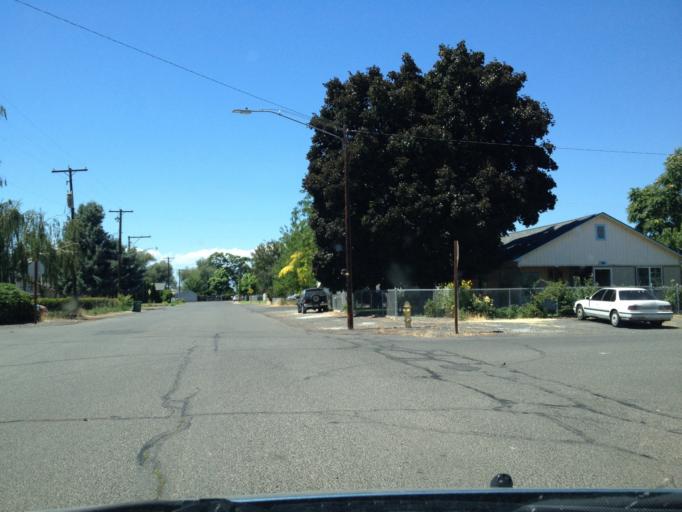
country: US
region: Washington
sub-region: Yakima County
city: Union Gap
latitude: 46.5467
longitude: -120.4776
